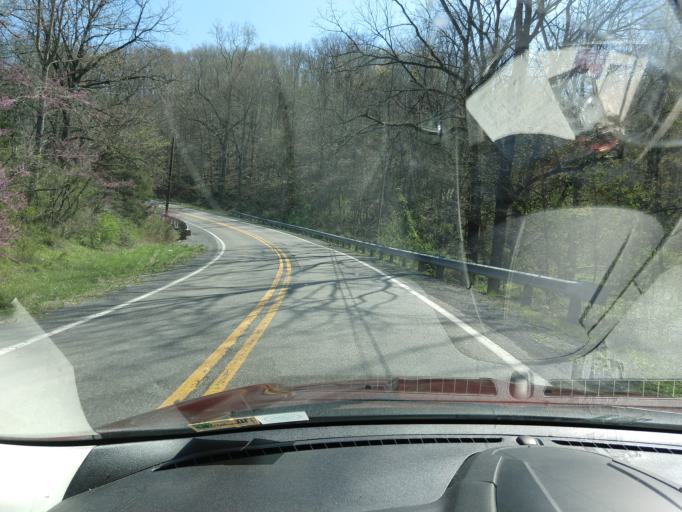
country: US
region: West Virginia
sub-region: Greenbrier County
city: Ronceverte
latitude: 37.7542
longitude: -80.5352
